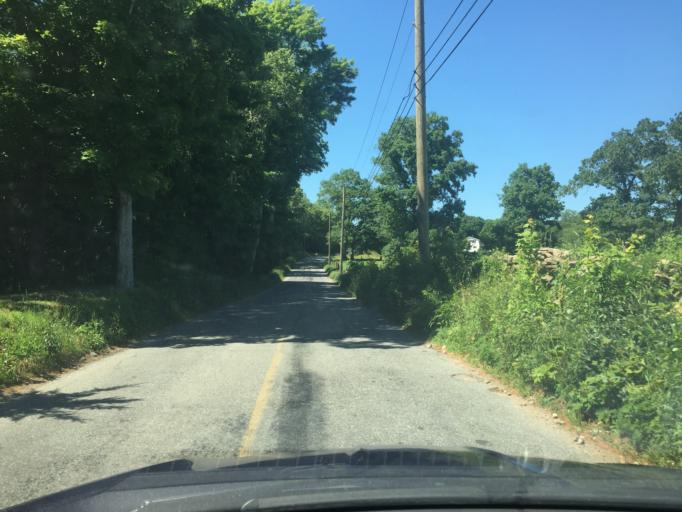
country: US
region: Rhode Island
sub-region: Washington County
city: Hopkinton
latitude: 41.4582
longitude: -71.8149
